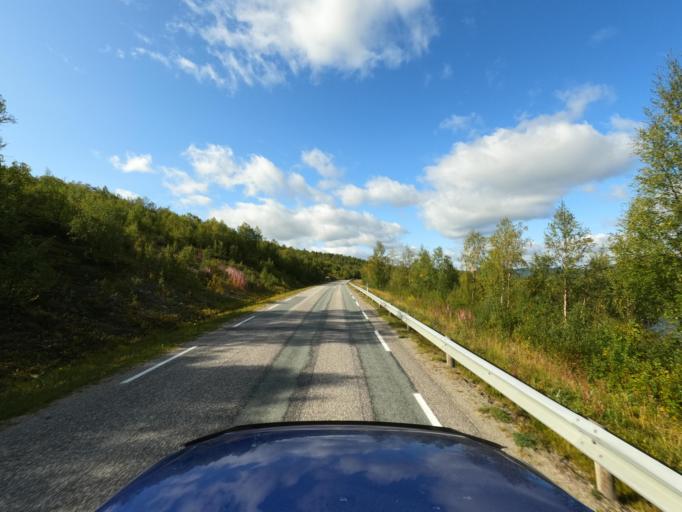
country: NO
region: Finnmark Fylke
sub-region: Karasjok
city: Karasjohka
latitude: 69.4360
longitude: 25.6793
